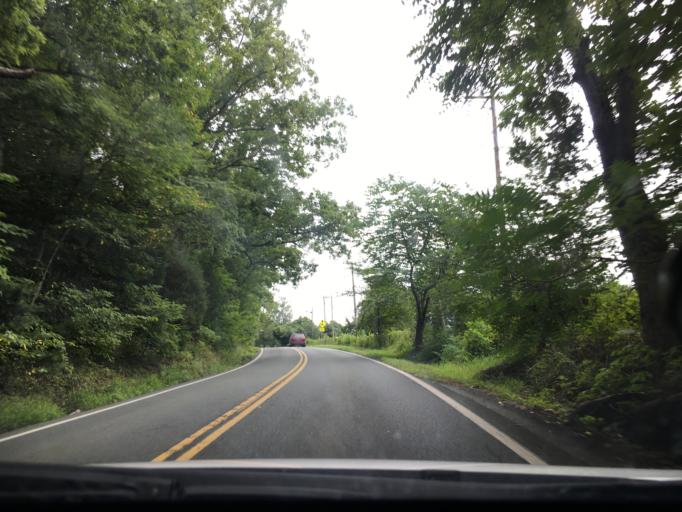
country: US
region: Virginia
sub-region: City of Charlottesville
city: Charlottesville
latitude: 37.9960
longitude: -78.4505
